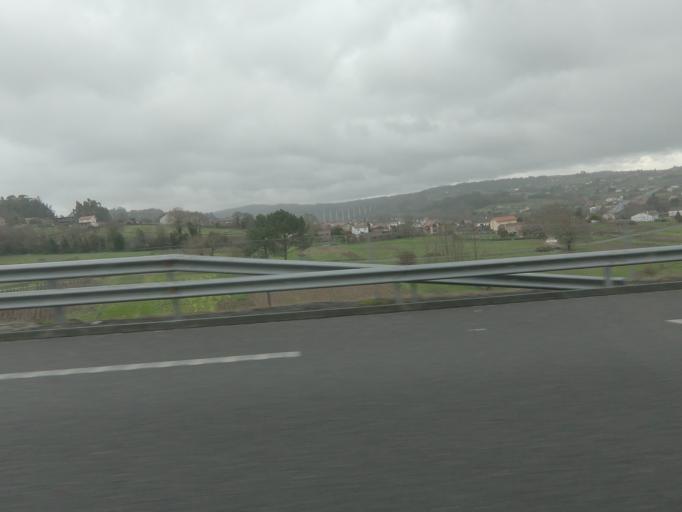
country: ES
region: Galicia
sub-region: Provincia da Coruna
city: Santiago de Compostela
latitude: 42.8463
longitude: -8.5327
